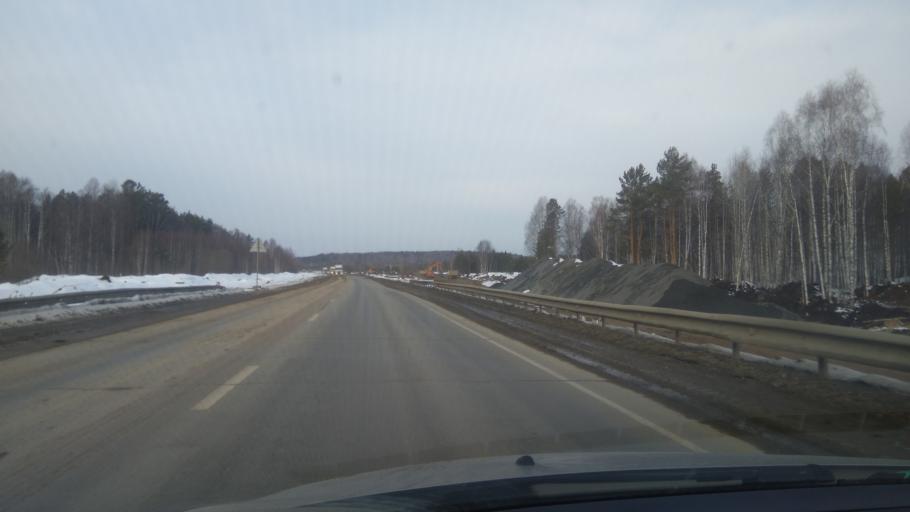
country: RU
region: Sverdlovsk
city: Bisert'
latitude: 56.8350
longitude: 58.9246
